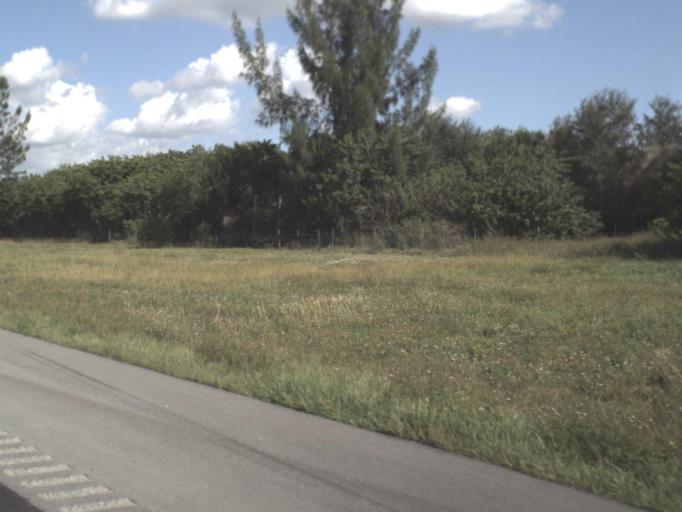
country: US
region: Florida
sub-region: Palm Beach County
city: Villages of Oriole
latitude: 26.4371
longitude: -80.1738
